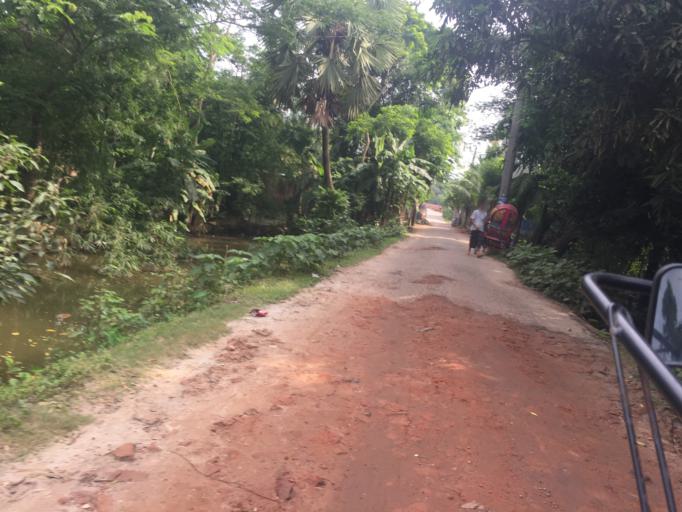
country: BD
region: Barisal
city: Mathba
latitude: 22.2152
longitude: 89.9132
